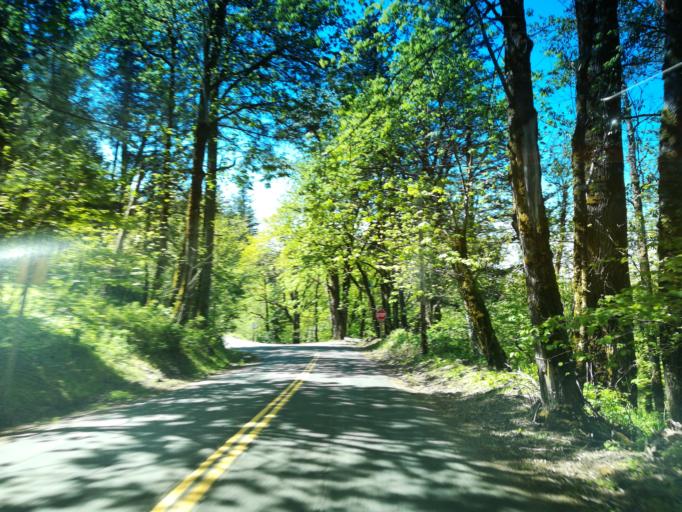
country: US
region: Oregon
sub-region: Multnomah County
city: Troutdale
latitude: 45.5097
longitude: -122.3656
